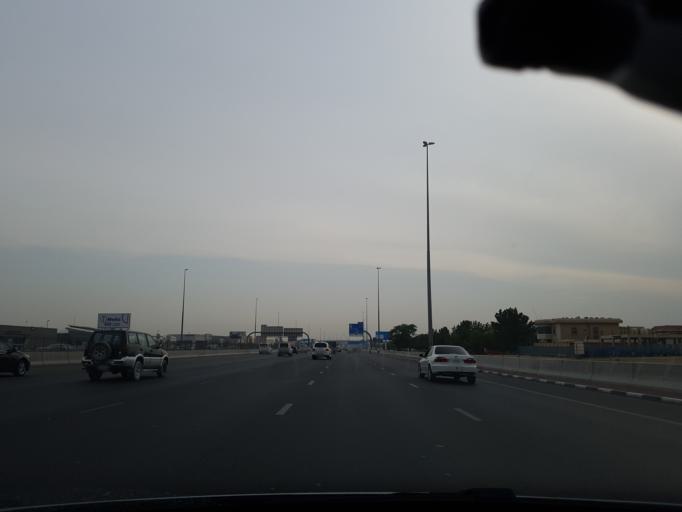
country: AE
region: Ash Shariqah
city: Sharjah
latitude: 25.3520
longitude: 55.4777
